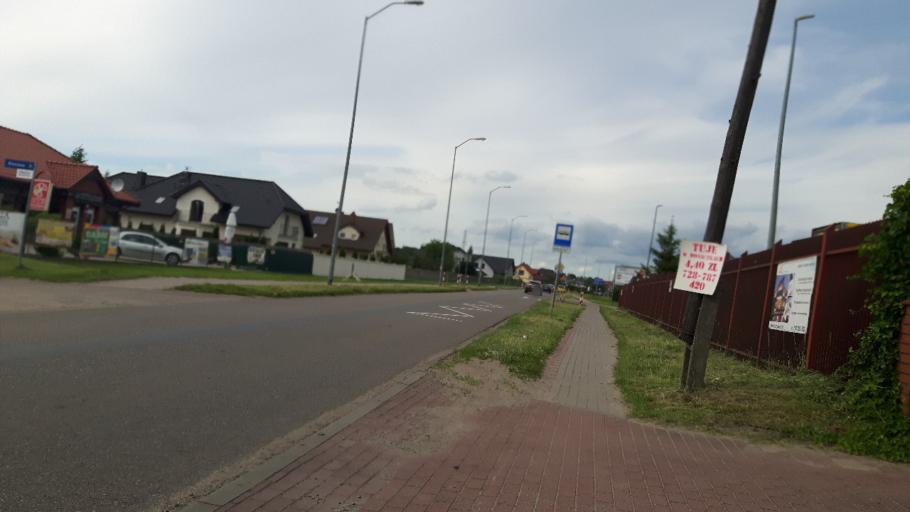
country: PL
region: West Pomeranian Voivodeship
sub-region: Powiat goleniowski
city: Goleniow
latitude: 53.4405
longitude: 14.7391
